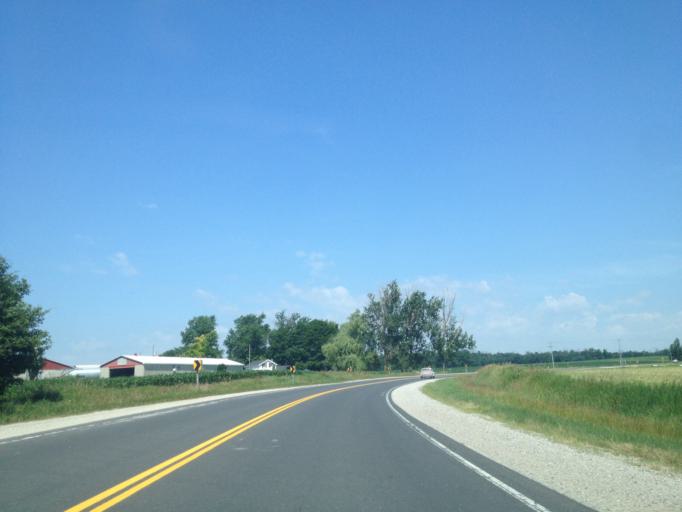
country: CA
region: Ontario
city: Huron East
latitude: 43.3735
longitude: -81.2163
